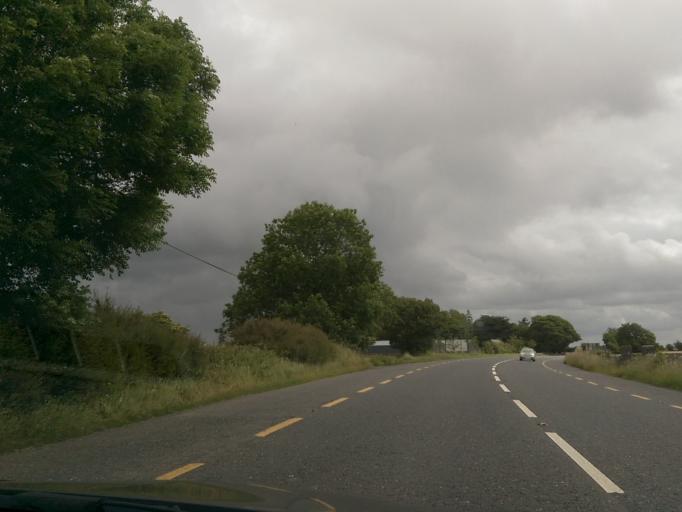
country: IE
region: Connaught
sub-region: County Galway
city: Loughrea
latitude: 53.2083
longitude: -8.5199
